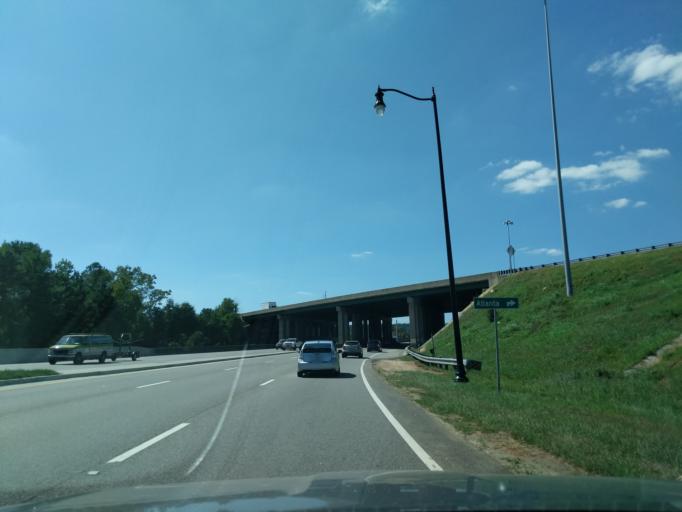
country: US
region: Georgia
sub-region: Columbia County
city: Martinez
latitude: 33.5215
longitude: -82.0295
